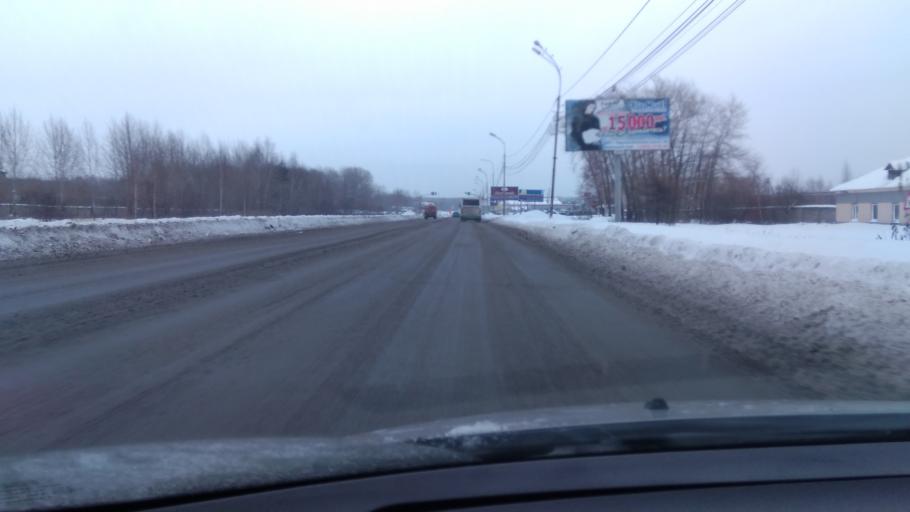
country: RU
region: Sverdlovsk
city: Nizhniy Tagil
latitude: 57.9090
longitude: 60.0184
